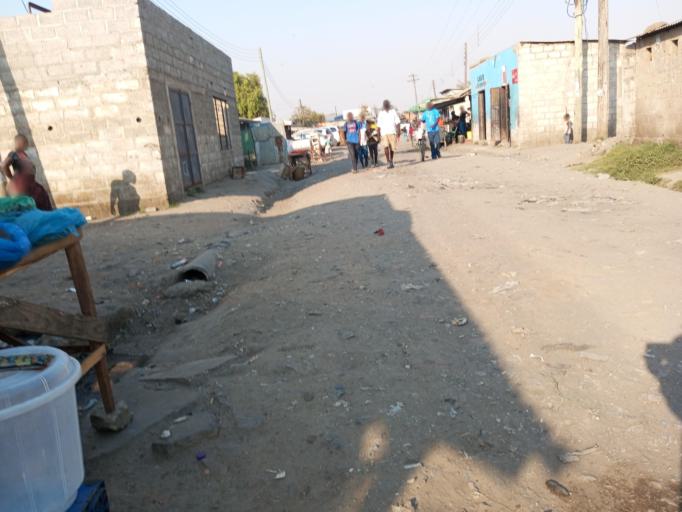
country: ZM
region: Lusaka
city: Lusaka
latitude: -15.3898
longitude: 28.2907
